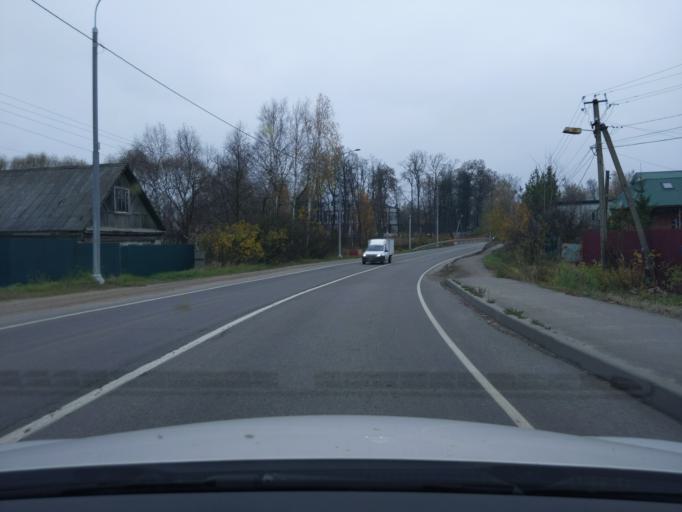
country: RU
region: Moskovskaya
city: Sofrino
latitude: 56.1230
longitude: 37.9671
